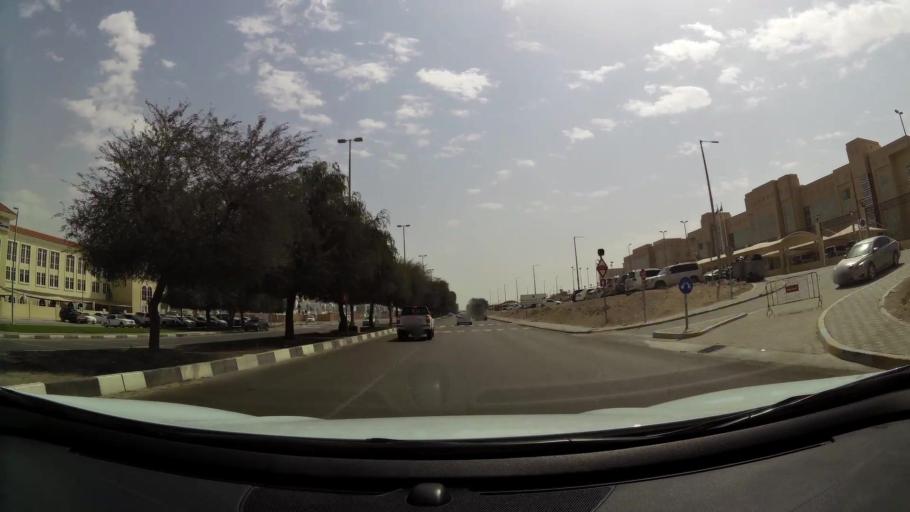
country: AE
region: Abu Dhabi
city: Abu Dhabi
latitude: 24.3066
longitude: 54.6191
